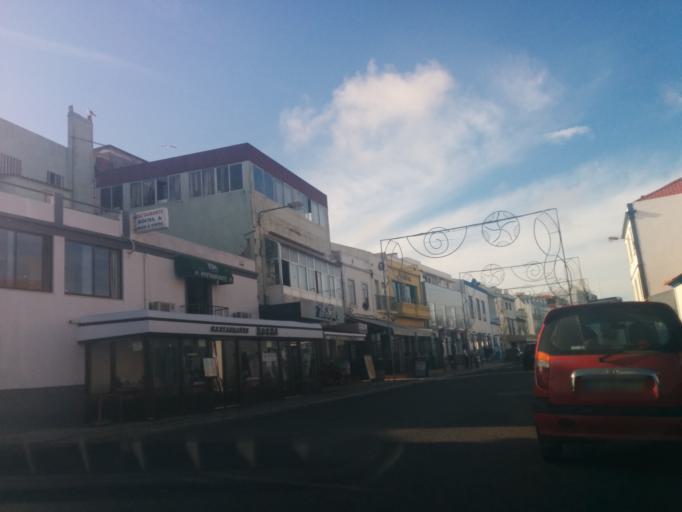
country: PT
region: Leiria
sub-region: Peniche
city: Peniche
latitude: 39.3538
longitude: -9.3789
